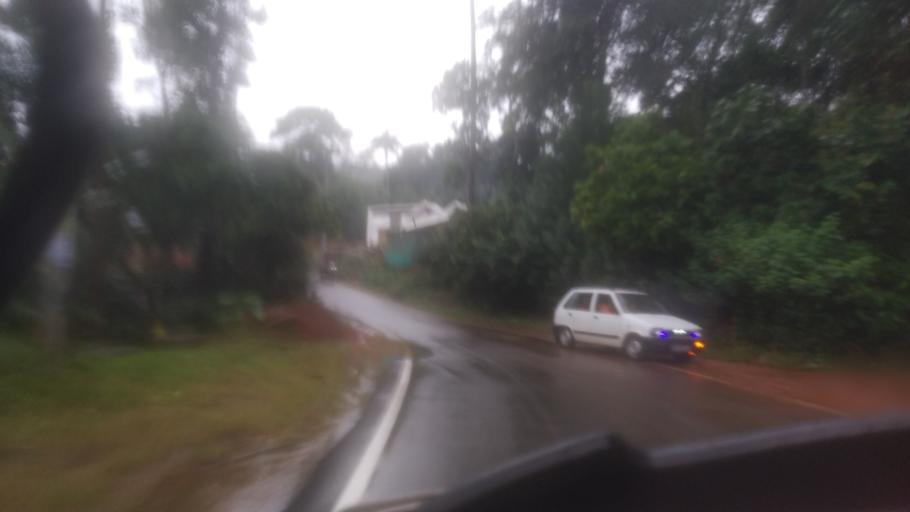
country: IN
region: Kerala
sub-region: Idukki
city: Idukki
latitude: 9.9296
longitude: 77.0705
